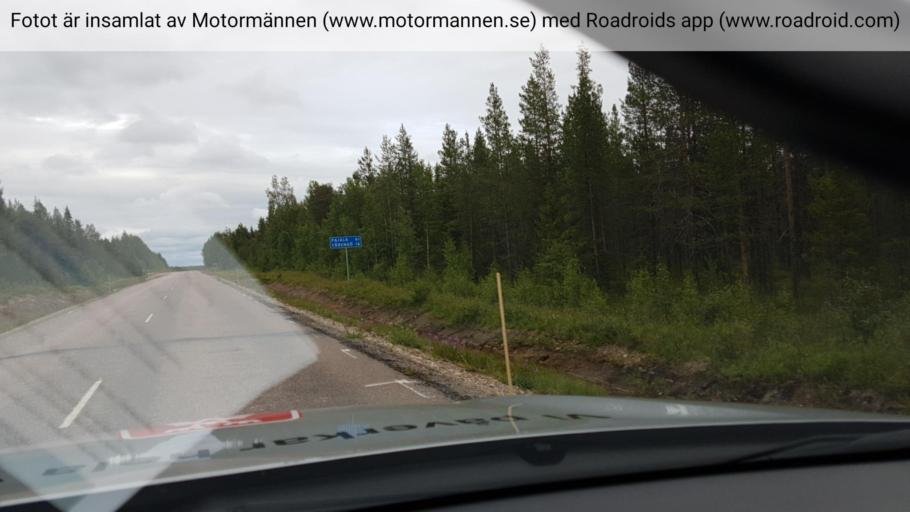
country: SE
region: Norrbotten
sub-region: Overkalix Kommun
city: OEverkalix
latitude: 67.0722
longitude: 22.4714
